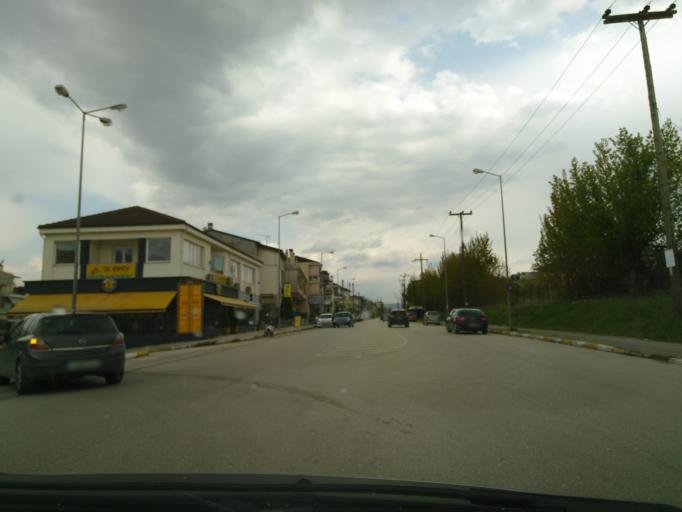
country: GR
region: Epirus
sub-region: Nomos Ioanninon
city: Anatoli
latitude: 39.6484
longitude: 20.8609
